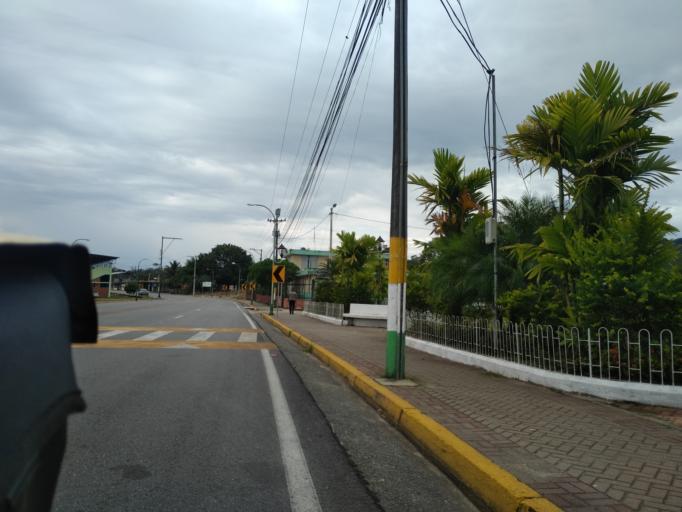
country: EC
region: Napo
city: Tena
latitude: -1.1726
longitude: -77.8568
